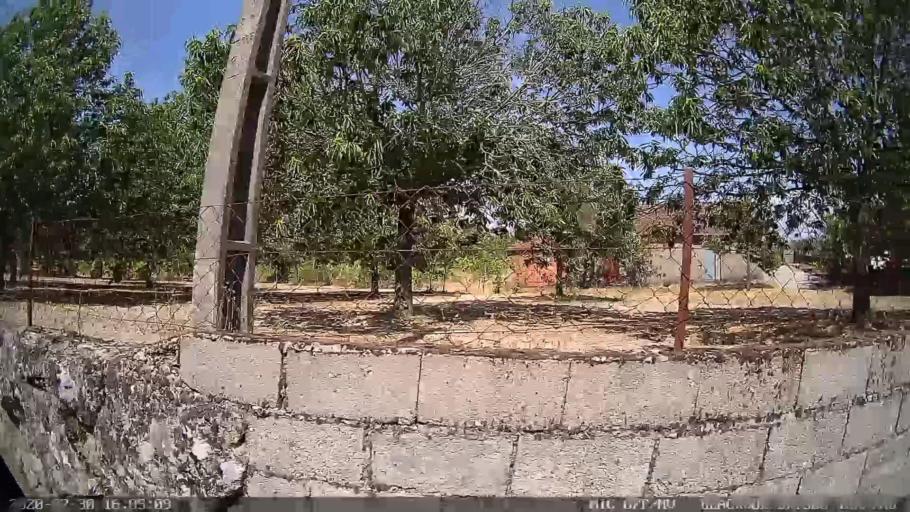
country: PT
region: Vila Real
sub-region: Murca
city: Murca
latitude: 41.3486
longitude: -7.4851
